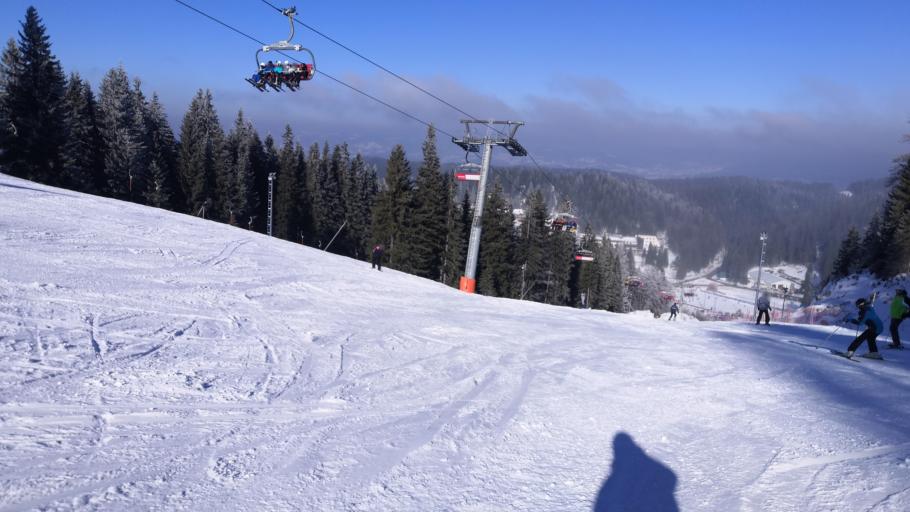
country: BA
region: Republika Srpska
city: Koran
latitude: 43.7320
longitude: 18.5651
